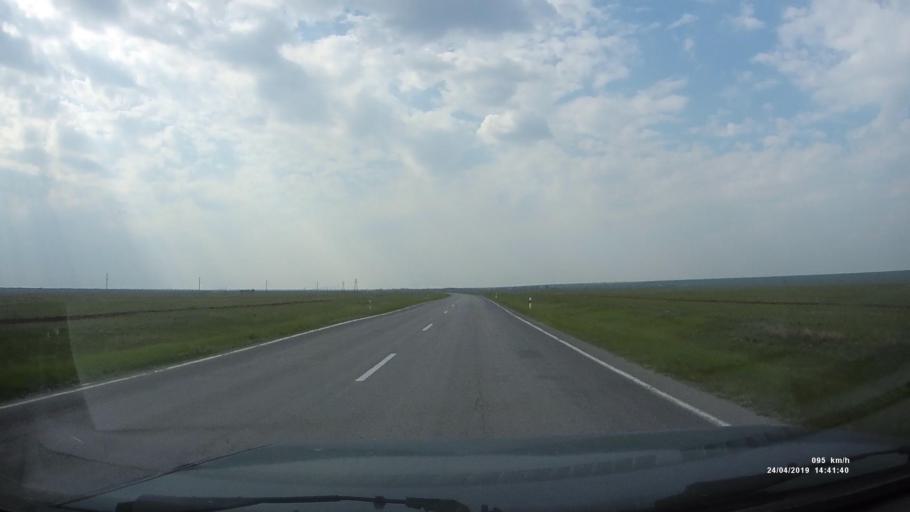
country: RU
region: Rostov
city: Remontnoye
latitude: 46.4470
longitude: 43.8762
